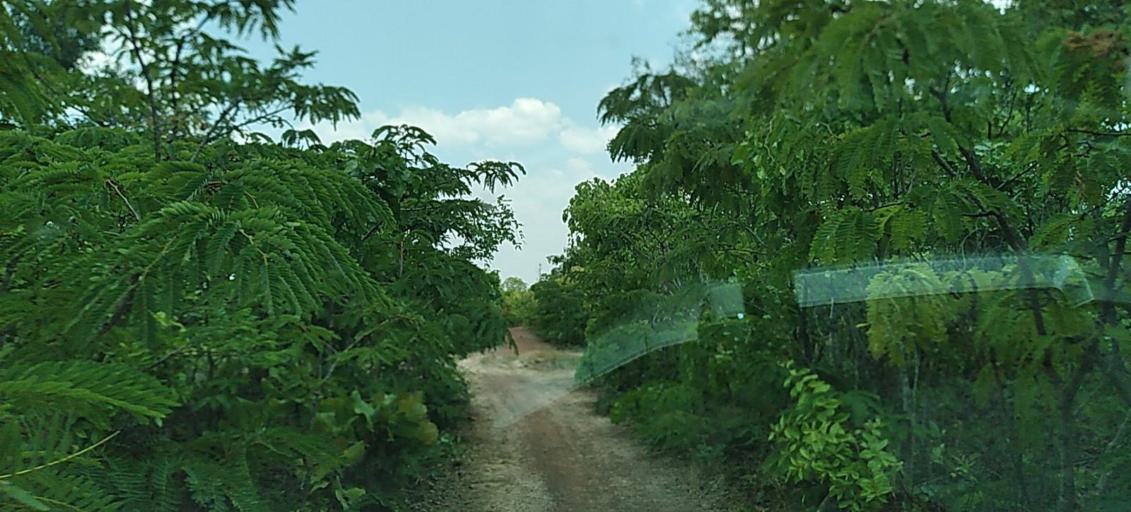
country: CD
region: Katanga
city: Kipushi
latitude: -12.0088
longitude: 27.4298
